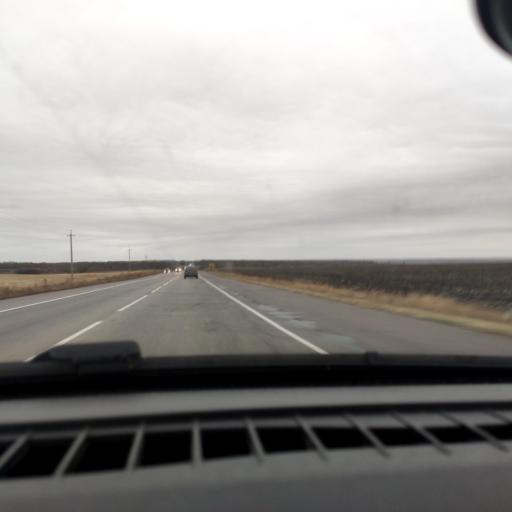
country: RU
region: Voronezj
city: Strelitsa
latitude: 51.5295
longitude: 38.9692
